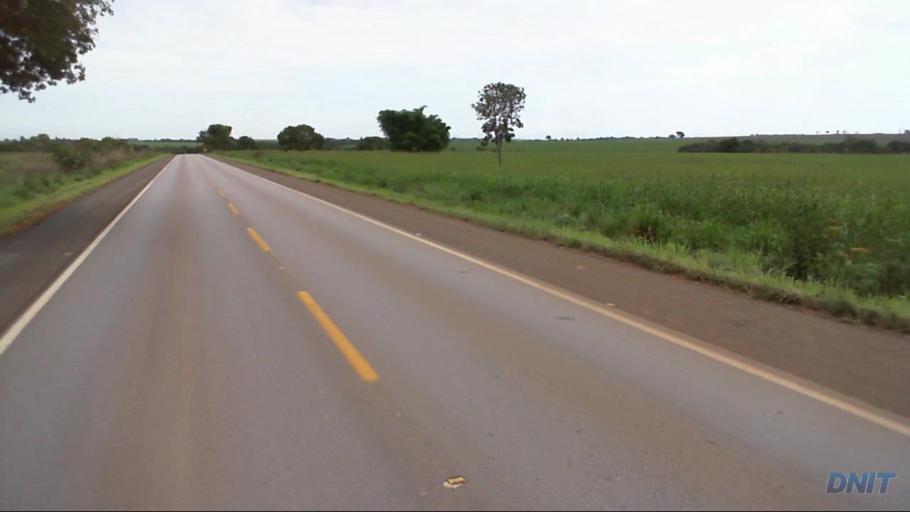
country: BR
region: Goias
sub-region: Uruacu
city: Uruacu
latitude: -14.7304
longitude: -49.0916
